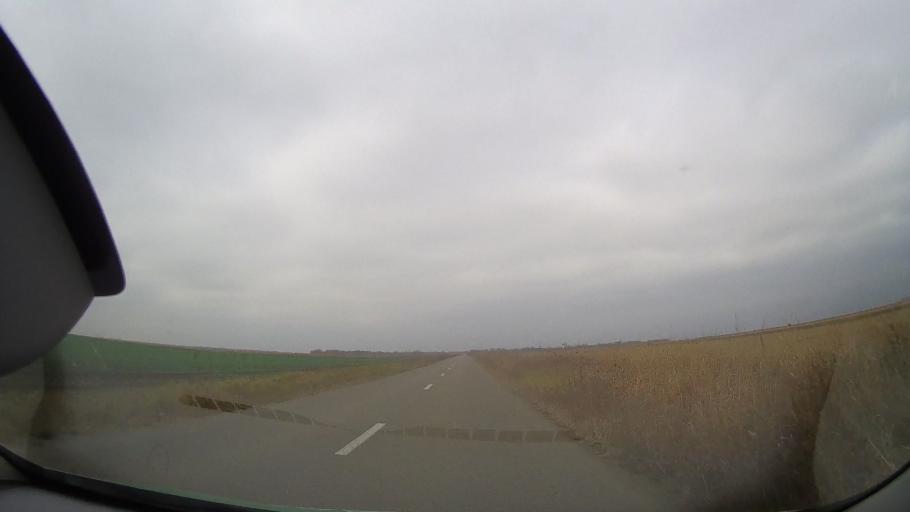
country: RO
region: Buzau
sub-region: Comuna Scutelnici
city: Scutelnici
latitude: 44.8642
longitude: 26.8962
